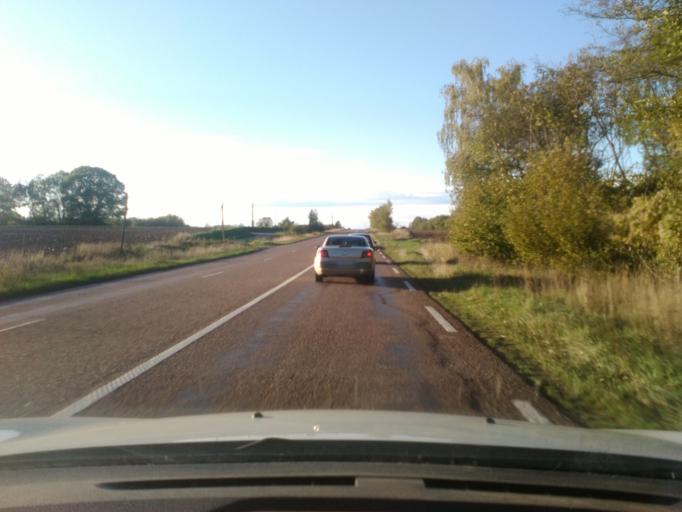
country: FR
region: Lorraine
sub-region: Departement des Vosges
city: Portieux
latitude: 48.3320
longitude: 6.3489
